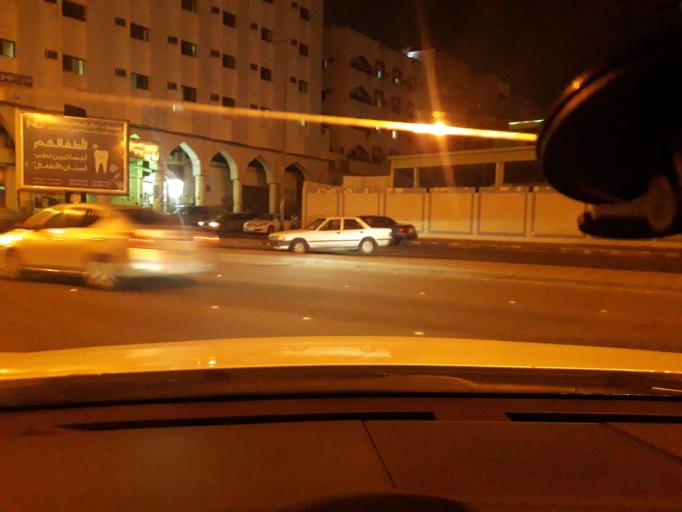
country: SA
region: Al Madinah al Munawwarah
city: Medina
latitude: 24.4584
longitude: 39.6143
